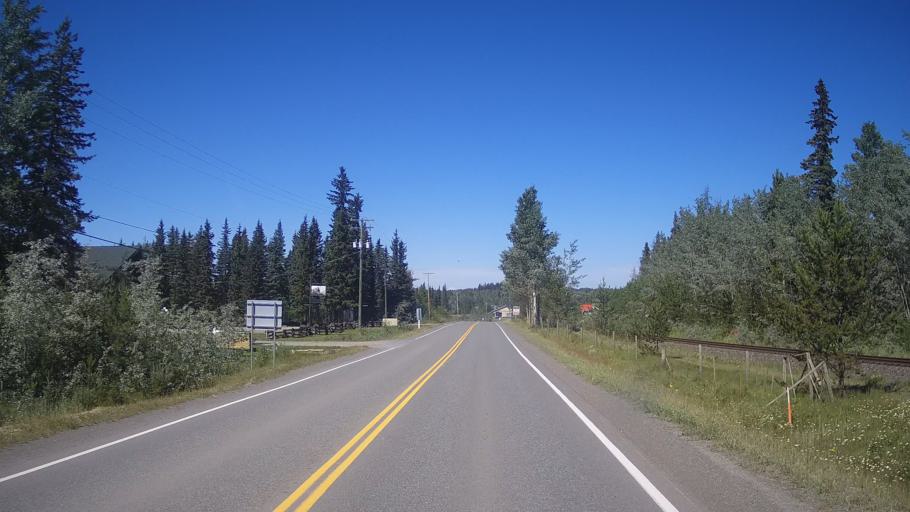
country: CA
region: British Columbia
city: Cache Creek
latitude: 51.5545
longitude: -121.1973
